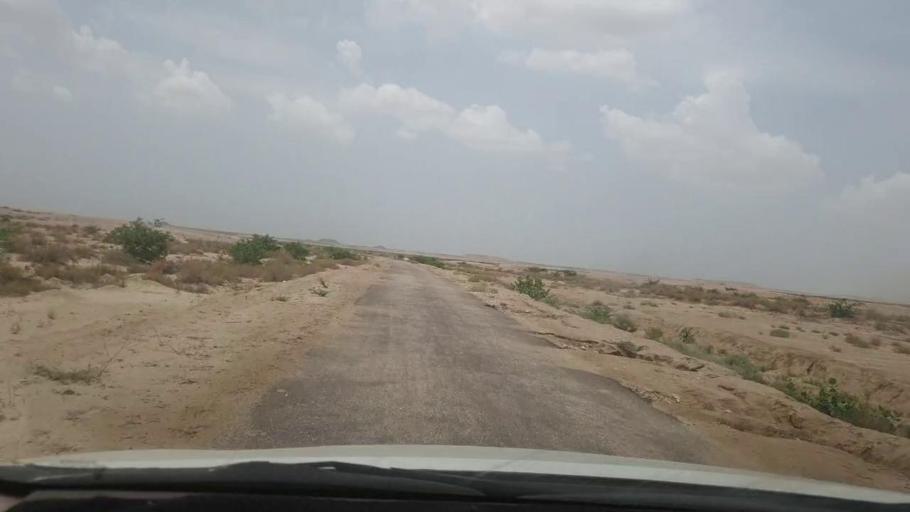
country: PK
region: Sindh
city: Khairpur
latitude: 27.3994
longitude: 68.9716
